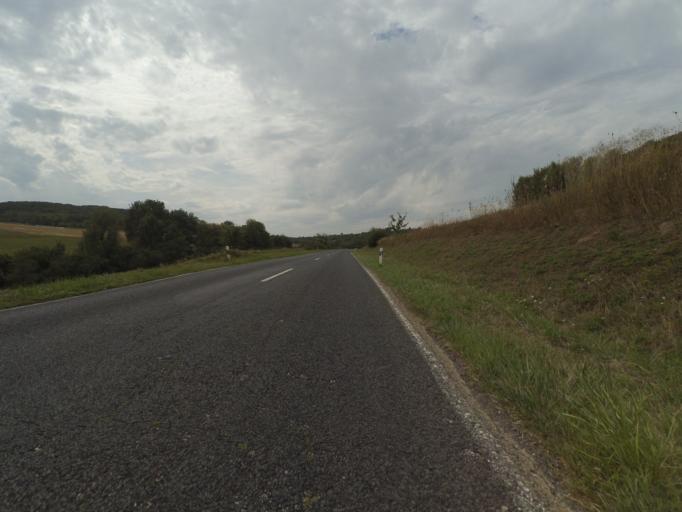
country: DE
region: Rheinland-Pfalz
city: Onsdorf
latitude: 49.6529
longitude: 6.4899
